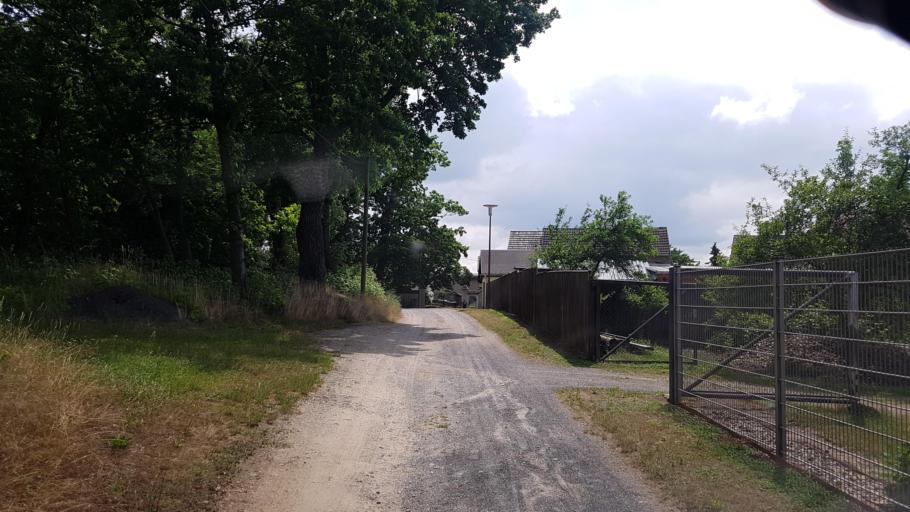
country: DE
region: Brandenburg
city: Crinitz
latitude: 51.7612
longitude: 13.8105
